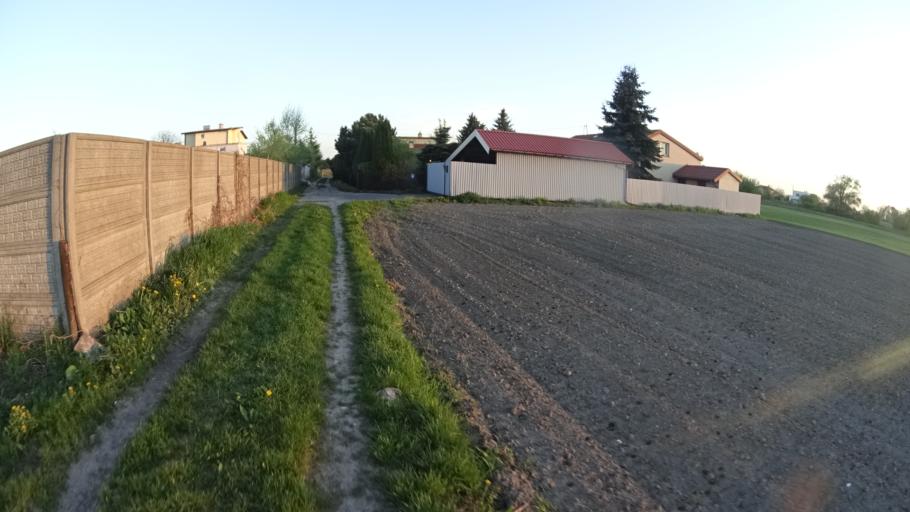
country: PL
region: Masovian Voivodeship
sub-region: Powiat warszawski zachodni
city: Ozarow Mazowiecki
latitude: 52.2238
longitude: 20.7811
